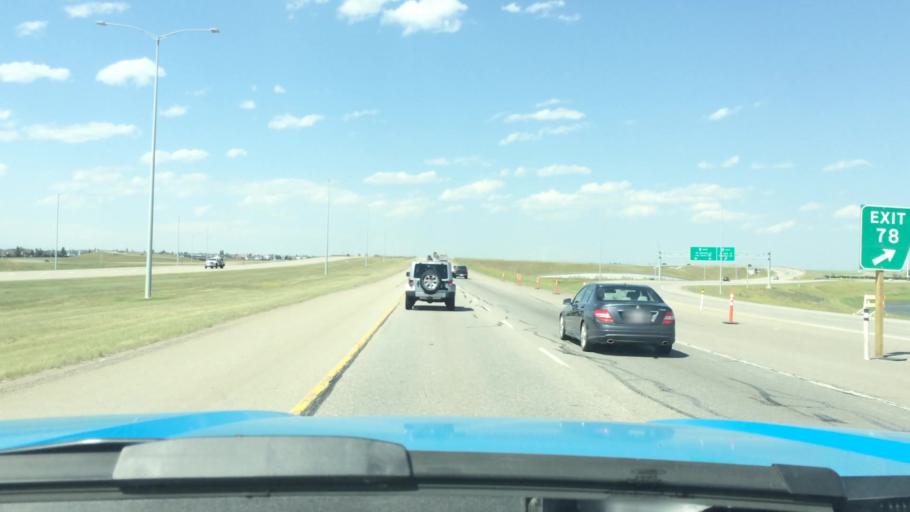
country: CA
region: Alberta
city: Chestermere
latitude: 51.0600
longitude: -113.9202
